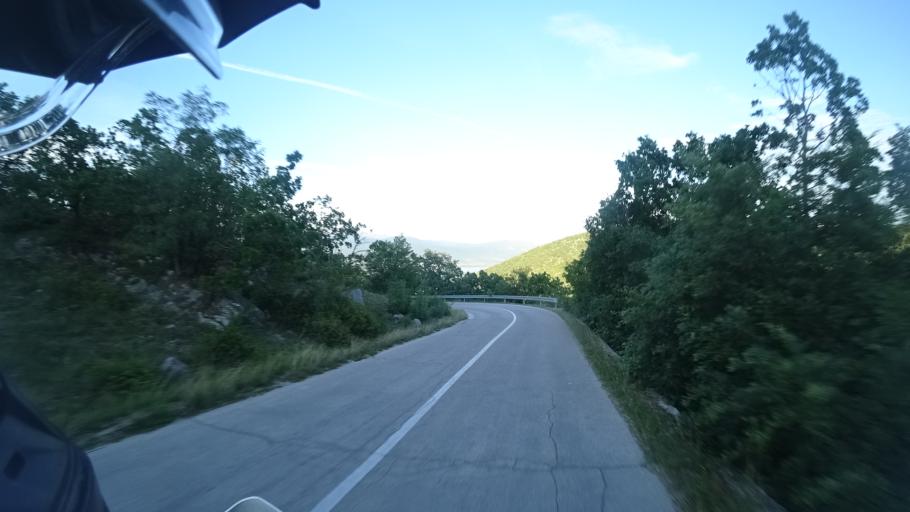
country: HR
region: Sibensko-Kniniska
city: Knin
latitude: 43.9012
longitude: 16.3973
